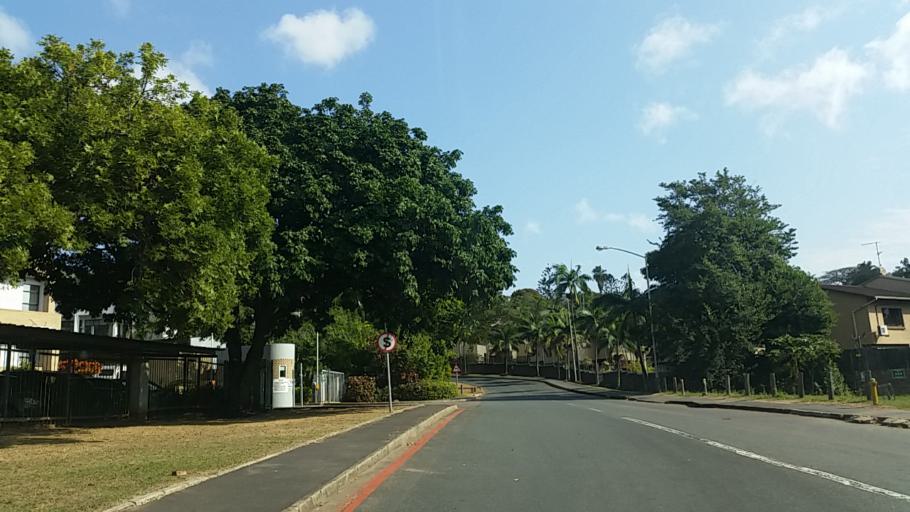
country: ZA
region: KwaZulu-Natal
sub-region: eThekwini Metropolitan Municipality
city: Berea
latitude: -29.8331
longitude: 30.9155
